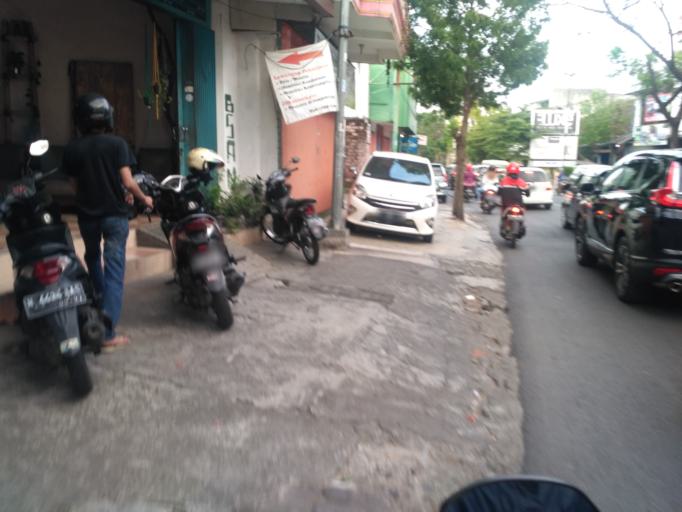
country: ID
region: East Java
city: Malang
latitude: -7.9729
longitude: 112.6287
